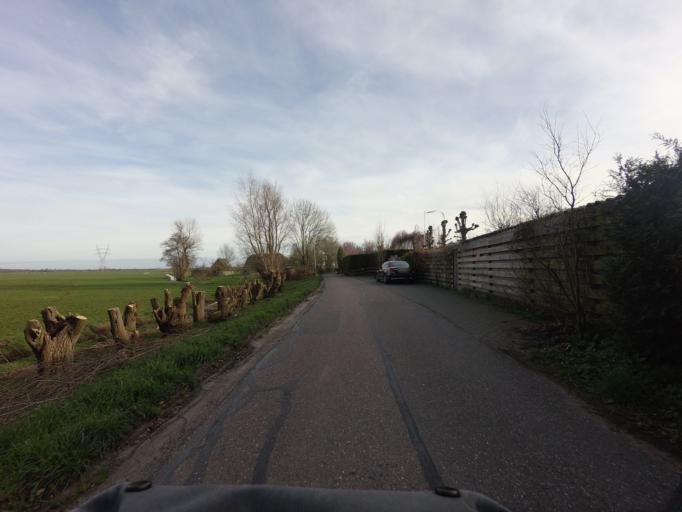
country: NL
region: North Holland
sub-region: Gemeente Weesp
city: Weesp
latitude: 52.3208
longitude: 5.0657
